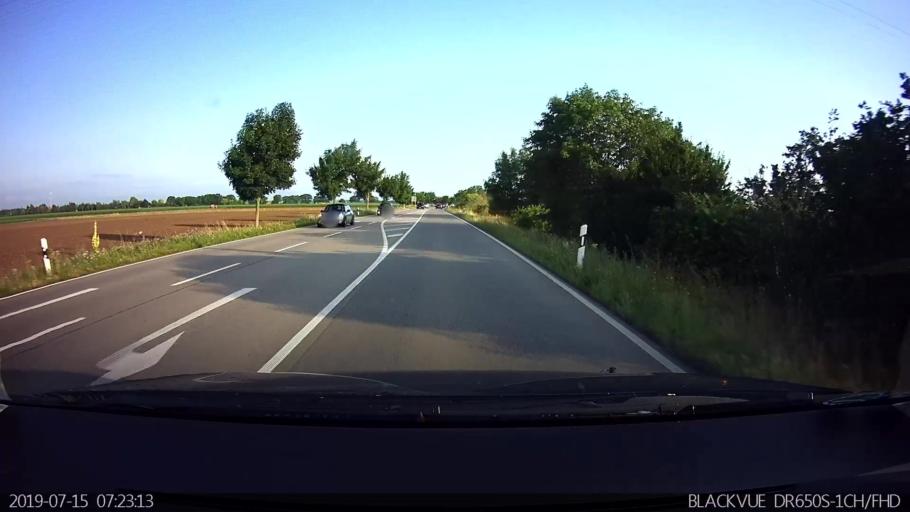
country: DE
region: Baden-Wuerttemberg
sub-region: Freiburg Region
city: Unterkrozingen
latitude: 47.9404
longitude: 7.6817
